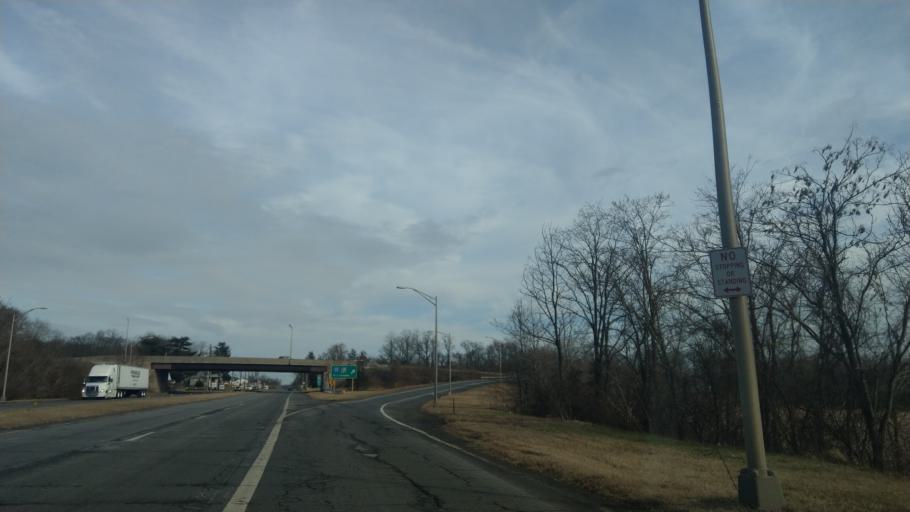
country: US
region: New Jersey
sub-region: Burlington County
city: Roebling
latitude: 40.1032
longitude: -74.7910
